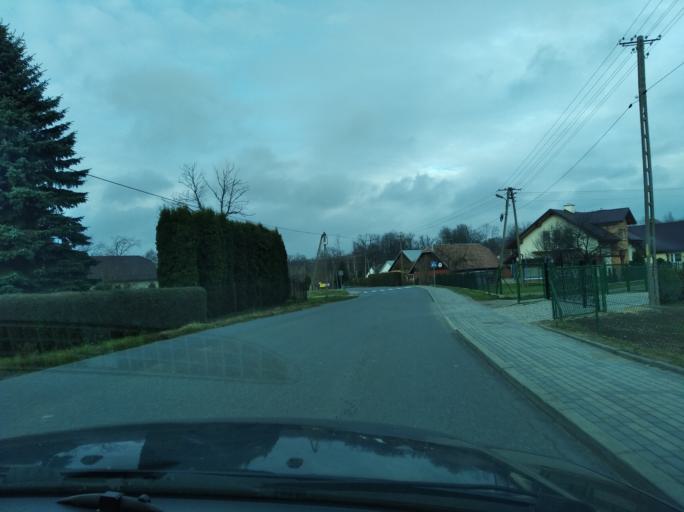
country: PL
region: Subcarpathian Voivodeship
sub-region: Powiat krosnienski
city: Kroscienko Wyzne
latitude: 49.6749
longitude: 21.8213
